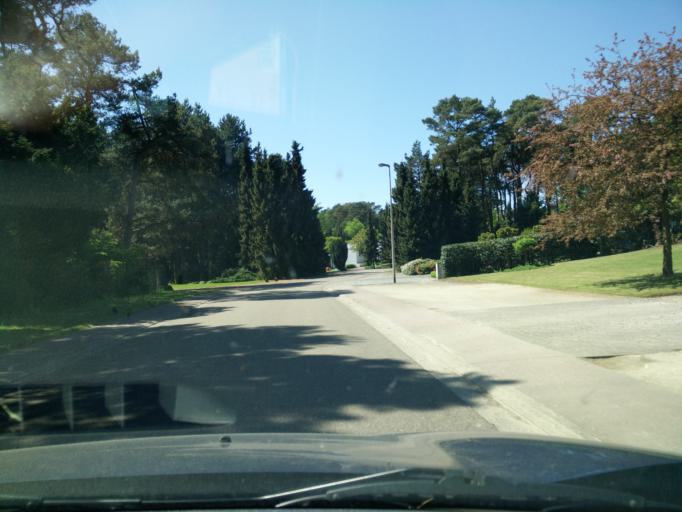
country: BE
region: Flanders
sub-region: Provincie Limburg
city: Maasmechelen
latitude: 50.9957
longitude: 5.6825
